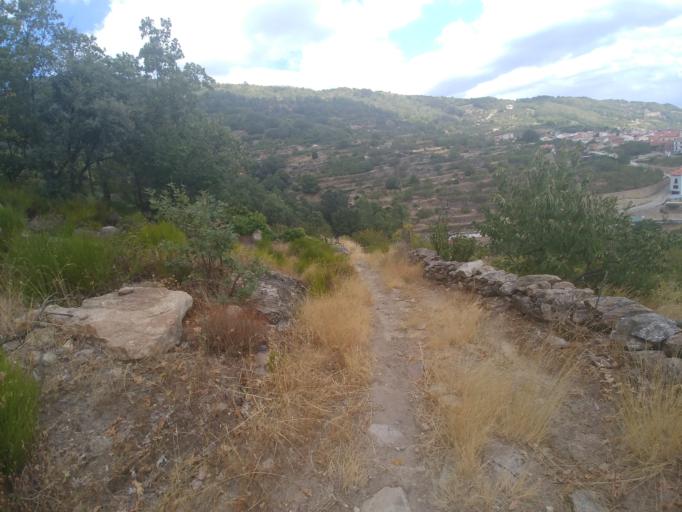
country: ES
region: Extremadura
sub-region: Provincia de Caceres
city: Cabezabellosa
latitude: 40.1338
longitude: -5.9501
